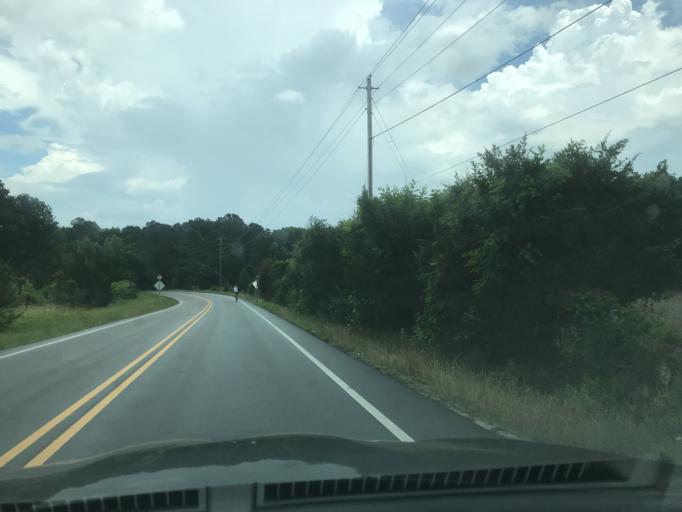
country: US
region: North Carolina
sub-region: Wake County
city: Knightdale
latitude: 35.8361
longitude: -78.4908
